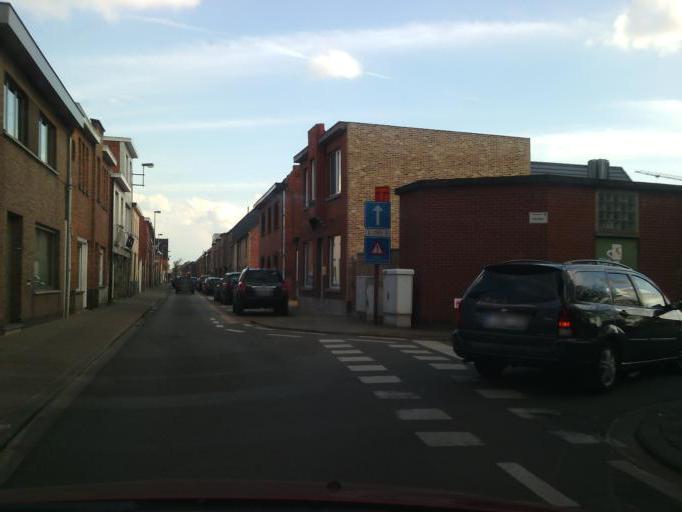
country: BE
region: Flanders
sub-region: Provincie Oost-Vlaanderen
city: Zele
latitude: 51.0655
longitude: 4.0221
